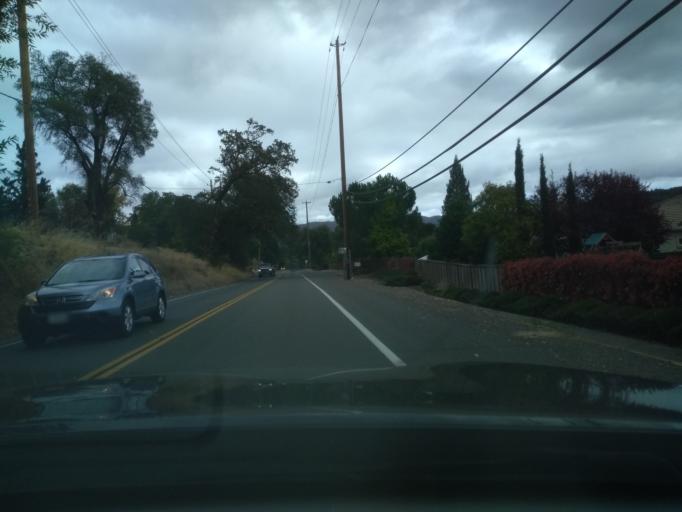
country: US
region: California
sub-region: Mendocino County
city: Ukiah
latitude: 39.1947
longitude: -123.2008
